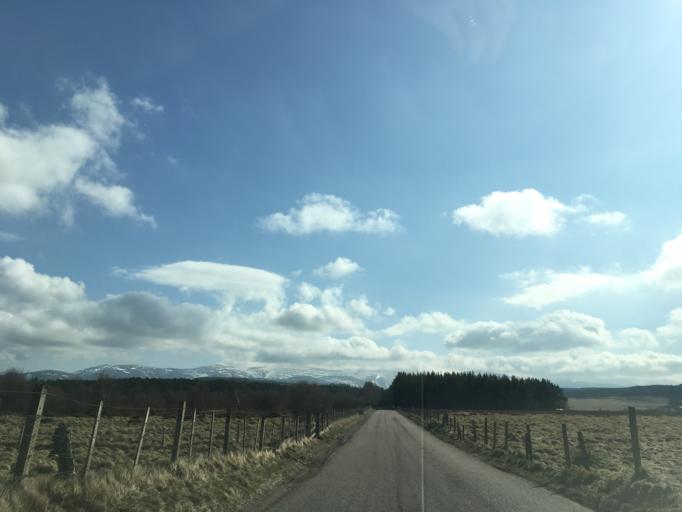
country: GB
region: Scotland
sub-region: Highland
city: Kingussie
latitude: 57.0710
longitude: -4.0126
